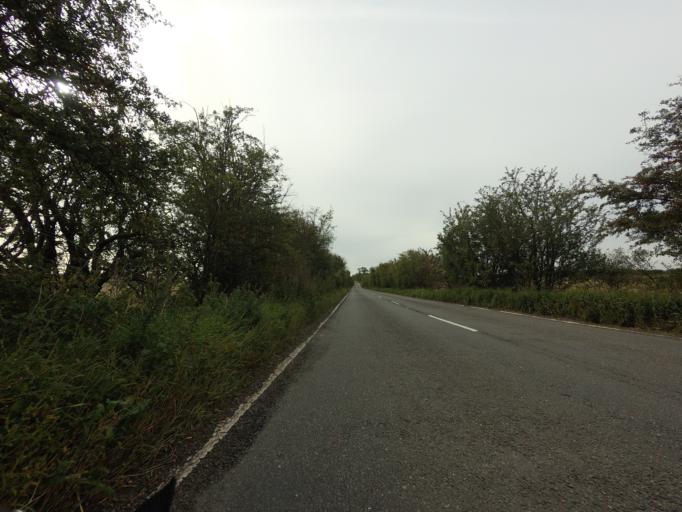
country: GB
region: England
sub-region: Cambridgeshire
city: Melbourn
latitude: 52.0404
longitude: 0.0426
